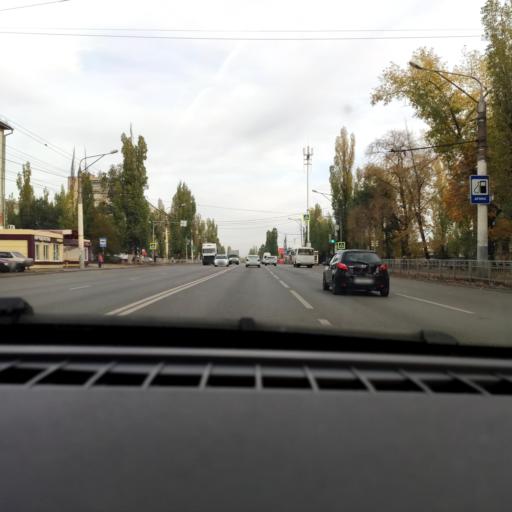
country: RU
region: Voronezj
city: Maslovka
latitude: 51.6090
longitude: 39.2373
